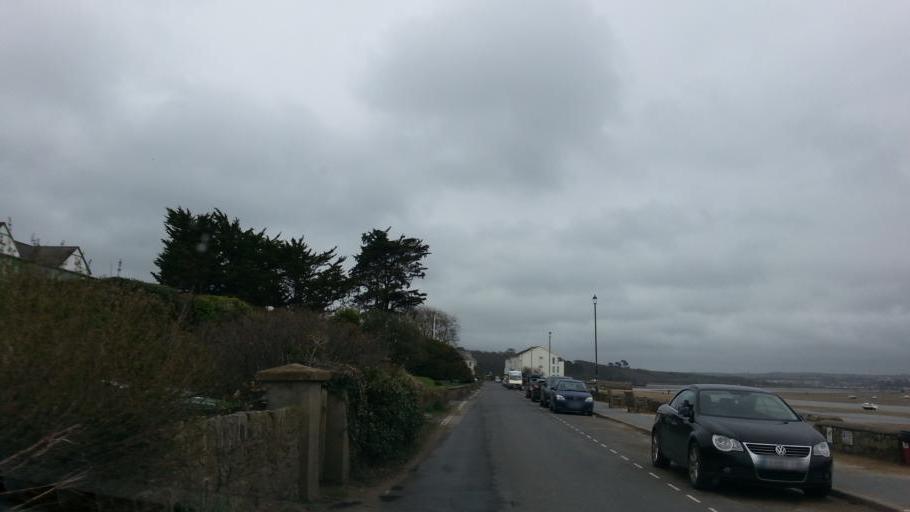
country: GB
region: England
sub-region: Devon
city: Appledore
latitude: 51.0542
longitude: -4.1813
